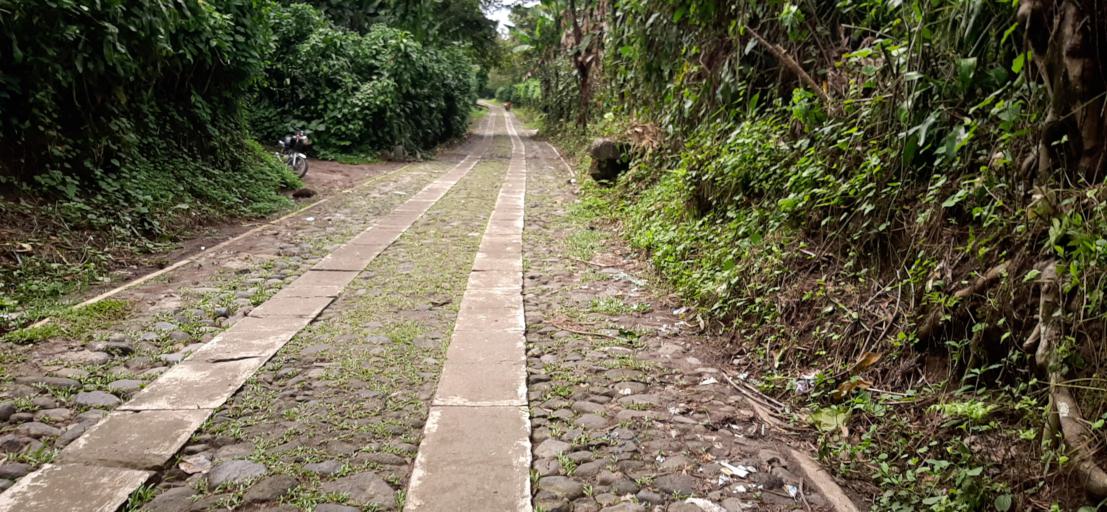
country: GT
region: Retalhuleu
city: San Martin Zapotitlan
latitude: 14.6081
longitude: -91.5757
